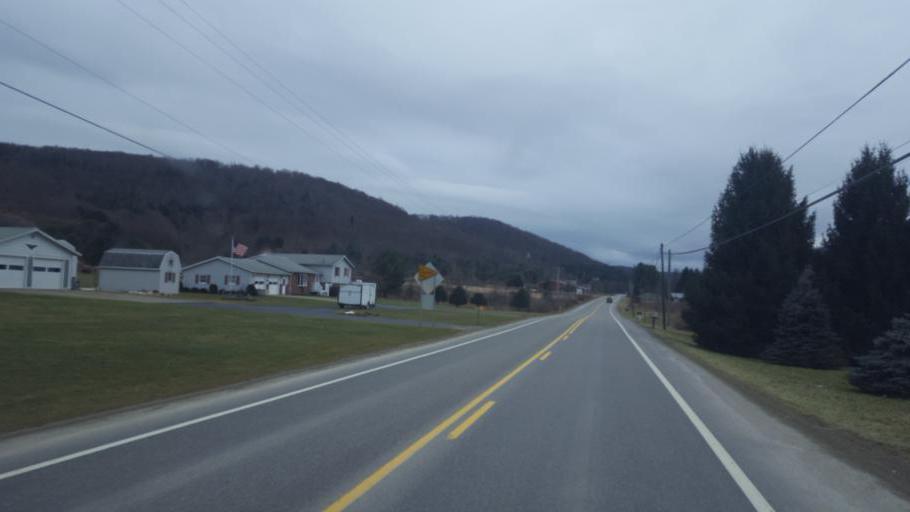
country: US
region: Pennsylvania
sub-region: Potter County
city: Coudersport
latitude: 41.7644
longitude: -78.1176
